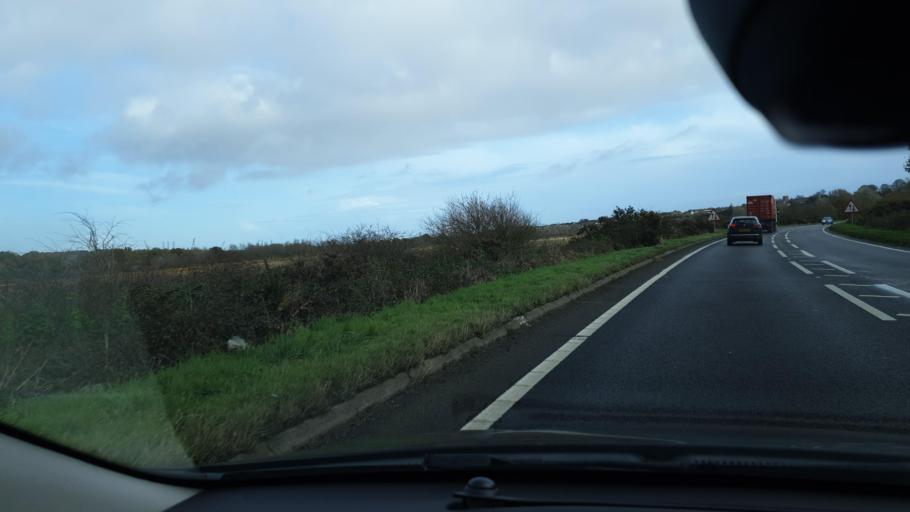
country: GB
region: England
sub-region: Suffolk
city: Shotley Gate
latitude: 51.9353
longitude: 1.2349
